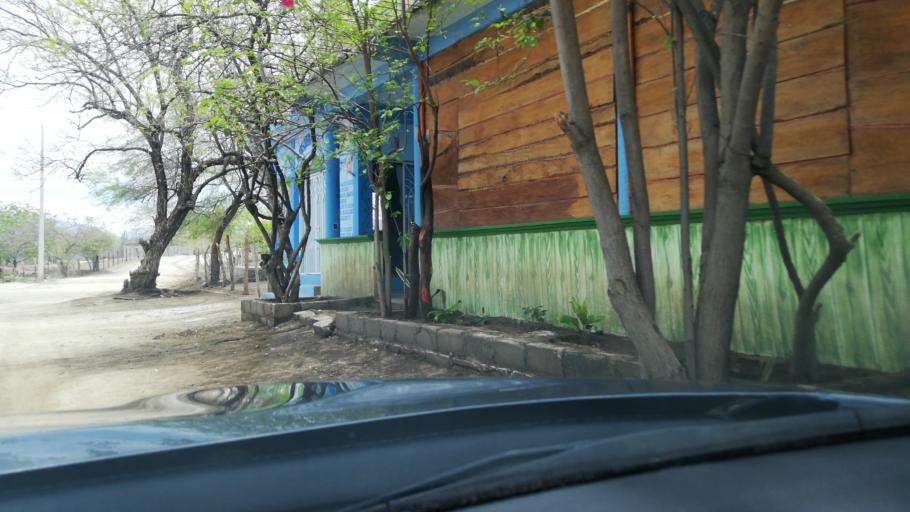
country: MX
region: Oaxaca
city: Santa Maria Jalapa del Marques
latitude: 16.4532
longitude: -95.4421
